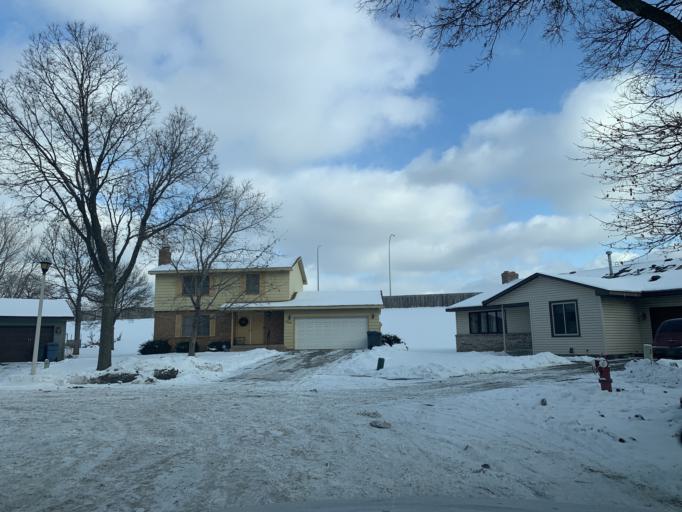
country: US
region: Minnesota
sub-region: Hennepin County
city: Minneapolis
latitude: 44.9941
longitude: -93.2858
